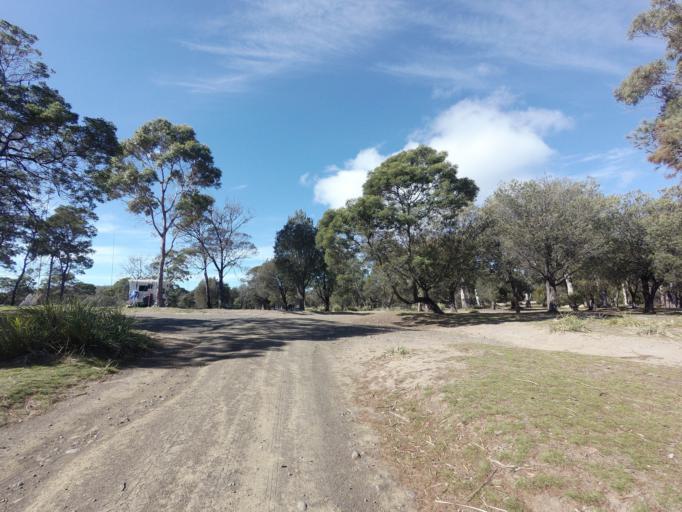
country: AU
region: Tasmania
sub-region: Clarence
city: Sandford
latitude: -42.9564
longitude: 147.7037
